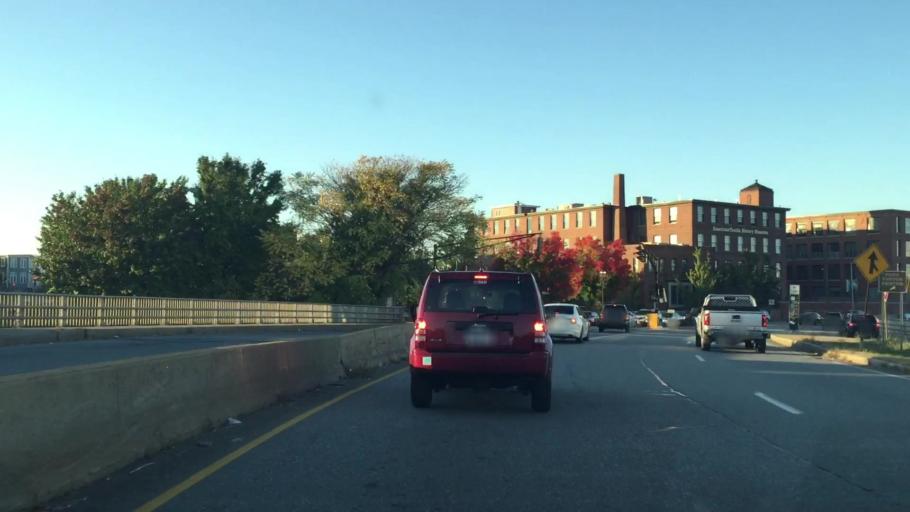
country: US
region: Massachusetts
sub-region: Middlesex County
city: Lowell
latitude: 42.6393
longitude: -71.3156
